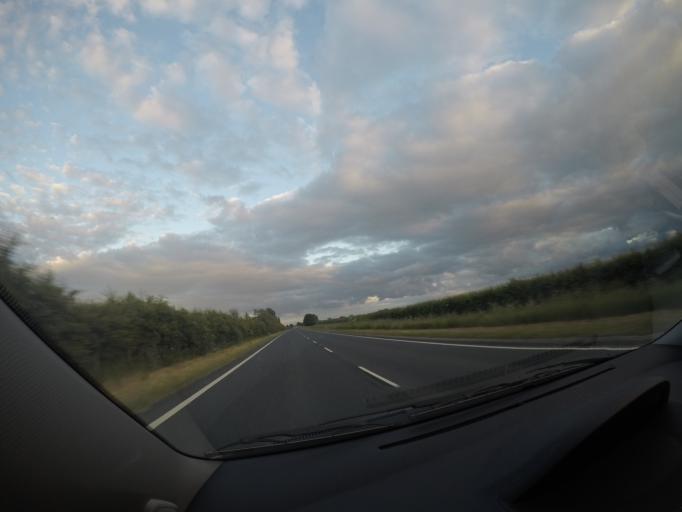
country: GB
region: England
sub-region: North Yorkshire
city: Bedale
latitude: 54.2519
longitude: -1.5094
